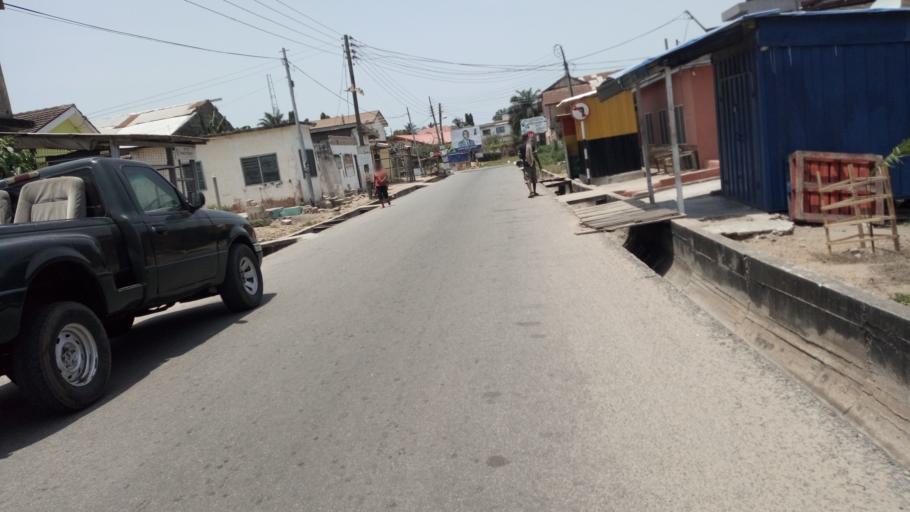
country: GH
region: Central
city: Winneba
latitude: 5.3467
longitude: -0.6269
